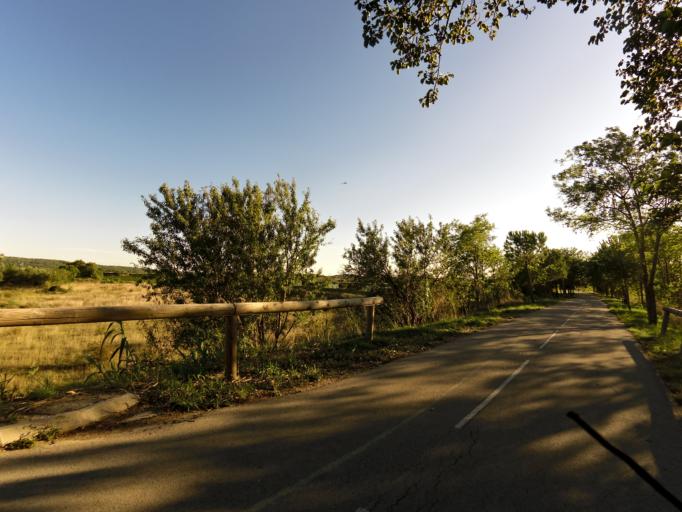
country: FR
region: Languedoc-Roussillon
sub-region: Departement du Gard
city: Calvisson
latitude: 43.7911
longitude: 4.2110
